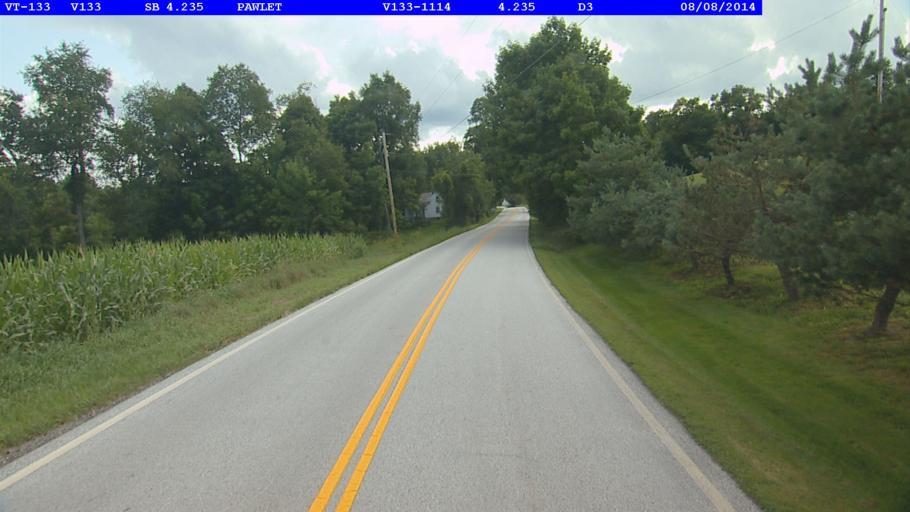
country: US
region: New York
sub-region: Washington County
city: Granville
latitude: 43.3898
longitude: -73.1333
